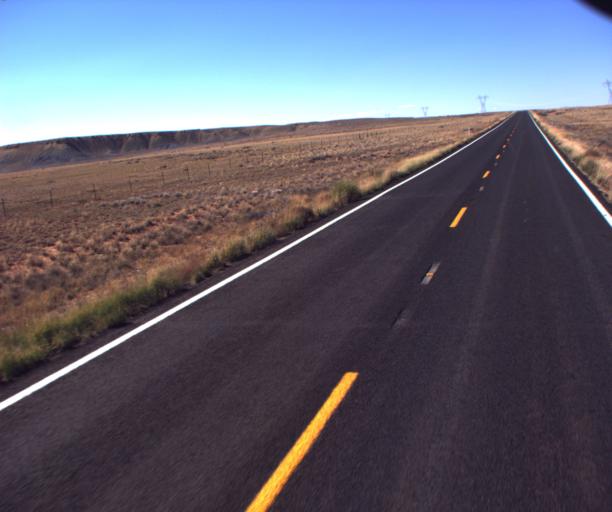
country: US
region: Arizona
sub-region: Coconino County
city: Tuba City
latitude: 35.9712
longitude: -110.8309
